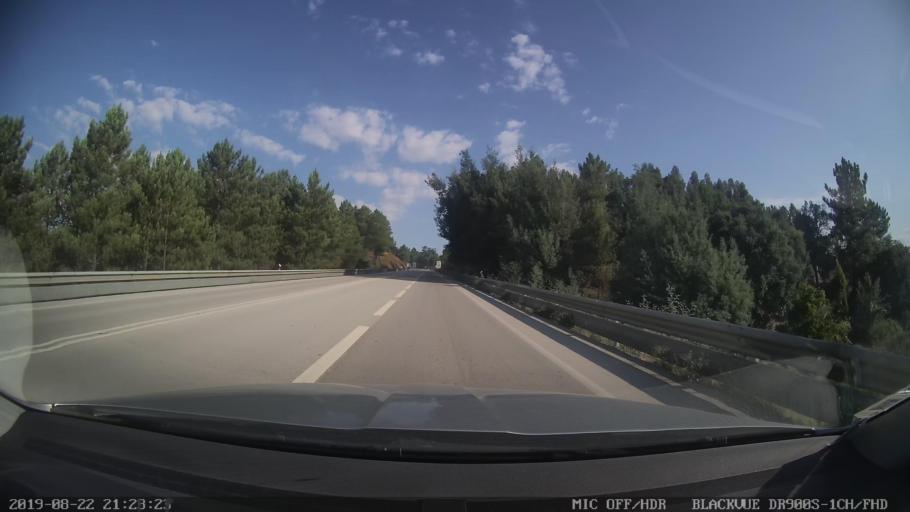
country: PT
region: Castelo Branco
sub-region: Serta
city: Serta
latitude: 39.8301
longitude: -8.1090
